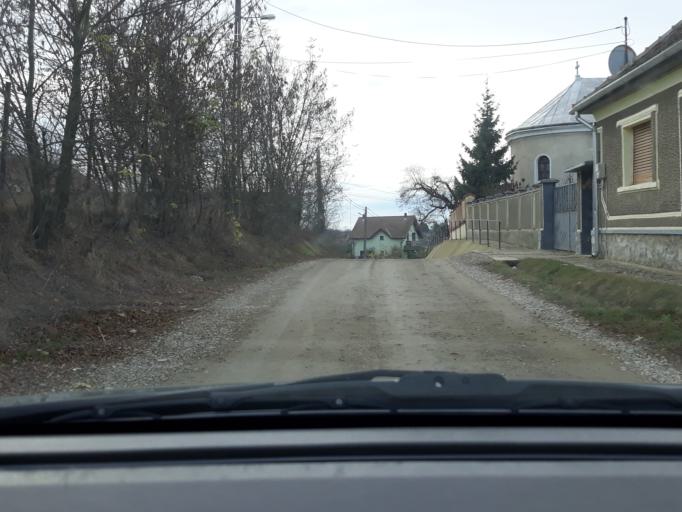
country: RO
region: Bihor
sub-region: Comuna Osorheiu
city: Alparea
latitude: 47.0130
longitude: 22.0211
